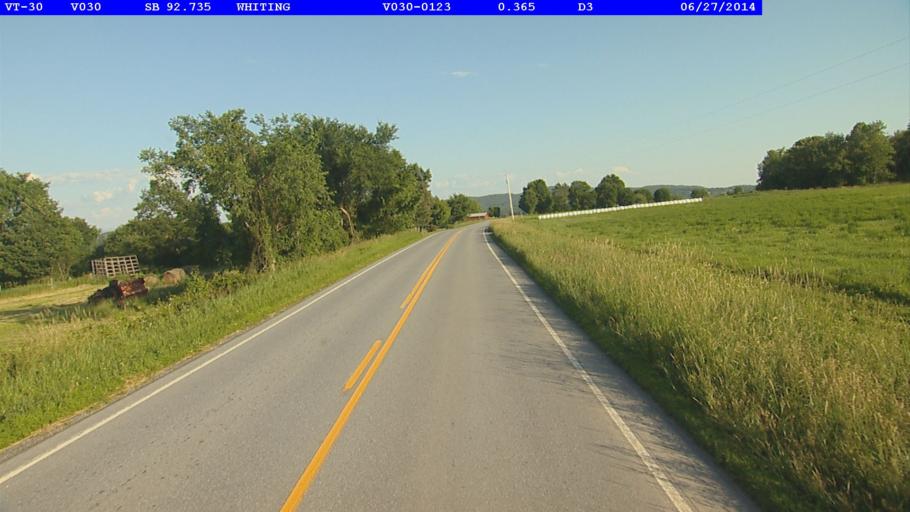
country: US
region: Vermont
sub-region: Rutland County
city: Brandon
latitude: 43.8434
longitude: -73.1959
